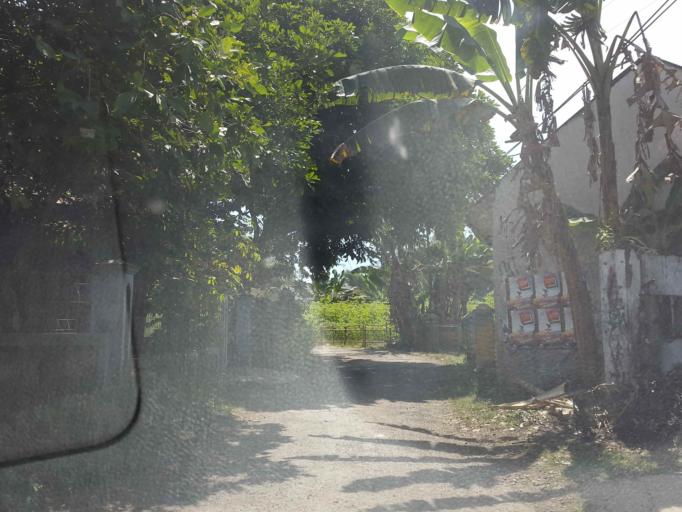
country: ID
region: West Java
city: Ciranjang-hilir
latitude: -6.8032
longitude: 107.3016
